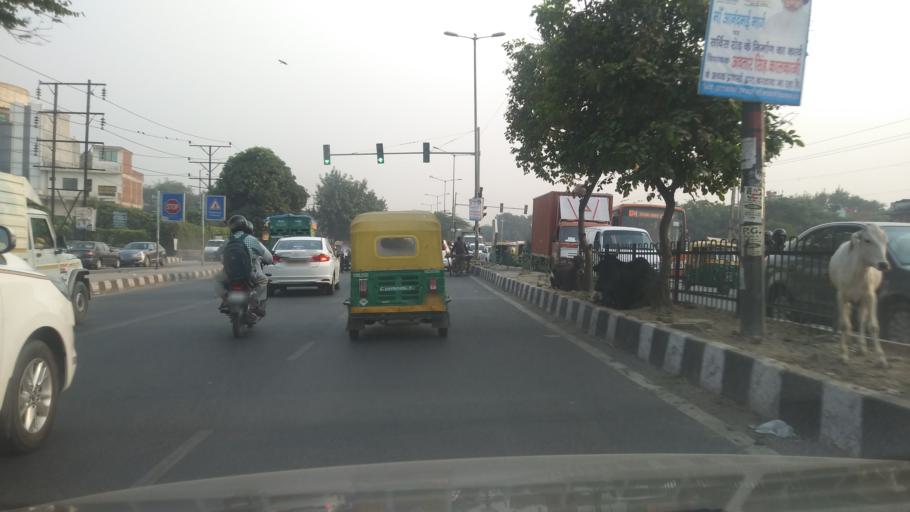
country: IN
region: Uttar Pradesh
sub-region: Gautam Buddha Nagar
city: Noida
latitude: 28.5336
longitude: 77.2688
